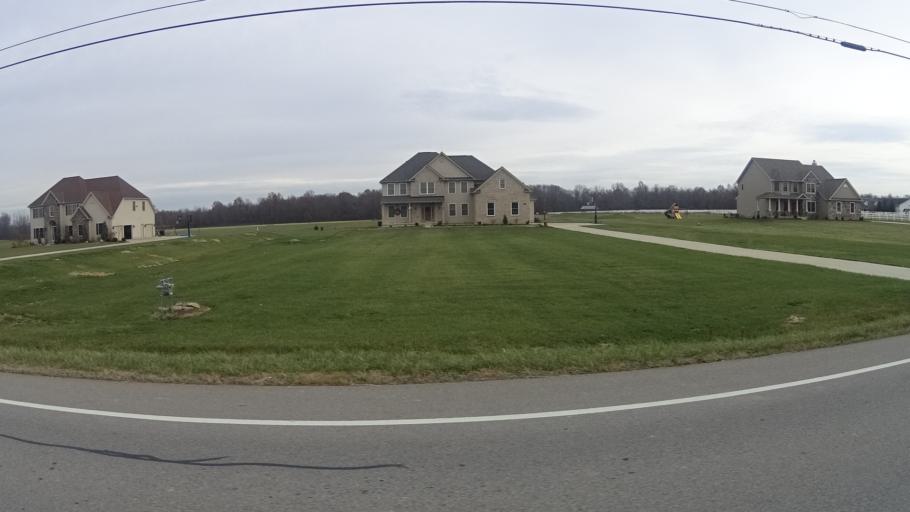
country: US
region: Ohio
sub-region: Lorain County
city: Eaton Estates
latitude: 41.2991
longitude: -81.9539
